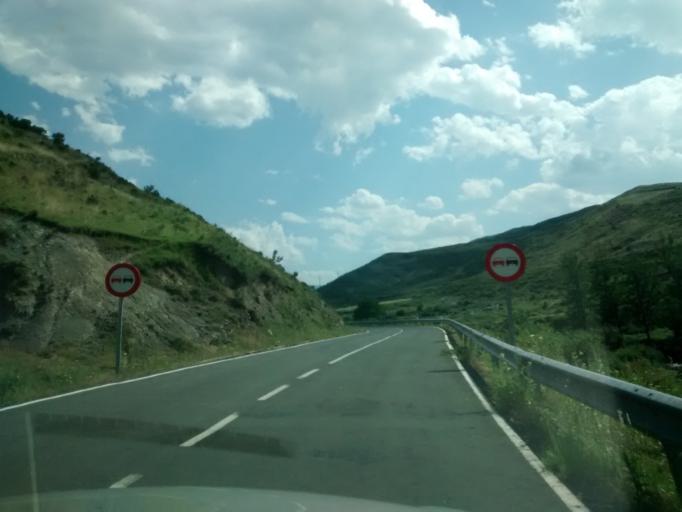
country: ES
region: La Rioja
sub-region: Provincia de La Rioja
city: Jalon de Cameros
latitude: 42.2182
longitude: -2.4775
